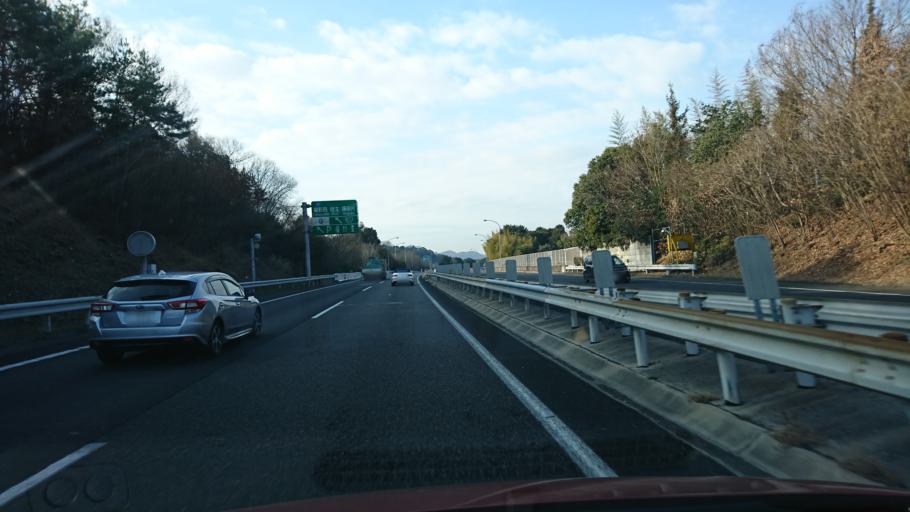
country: JP
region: Hyogo
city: Tatsunocho-tominaga
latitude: 34.8368
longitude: 134.5096
